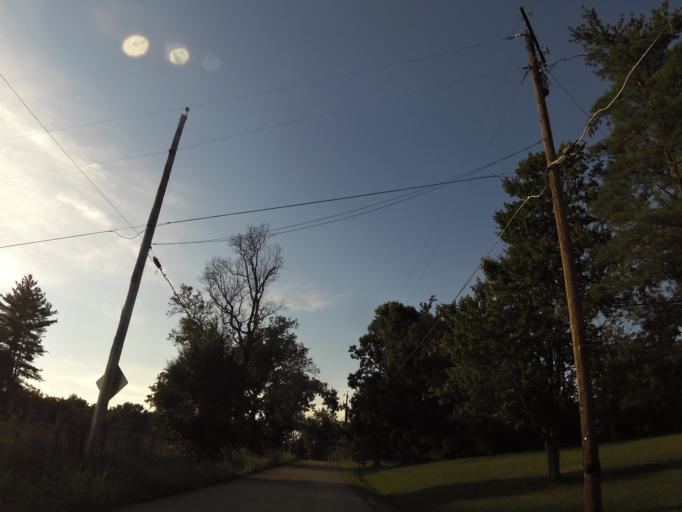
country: US
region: Tennessee
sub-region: Blount County
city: Eagleton Village
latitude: 35.8703
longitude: -83.9222
